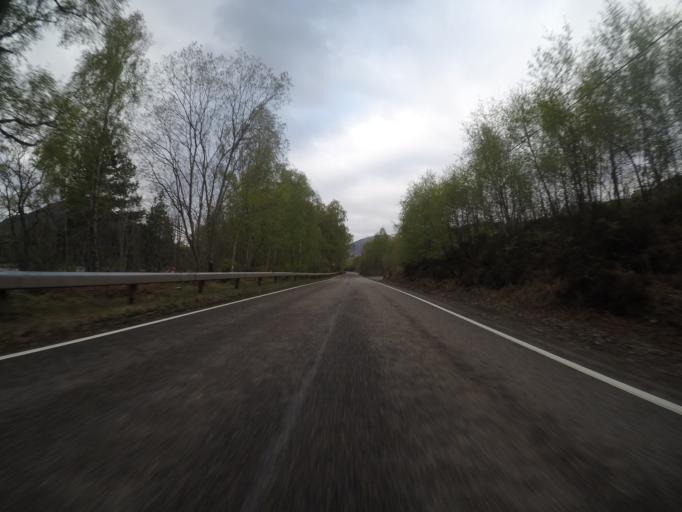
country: GB
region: Scotland
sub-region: Highland
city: Kingussie
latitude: 56.9585
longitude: -4.4670
